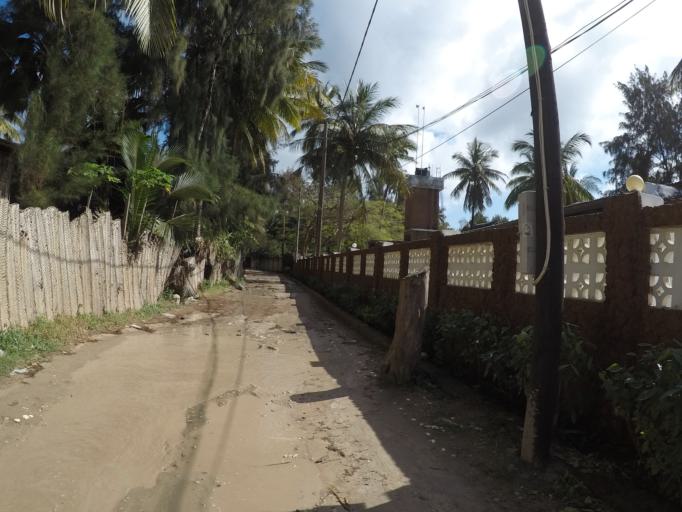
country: TZ
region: Zanzibar North
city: Nungwi
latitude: -5.7256
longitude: 39.2942
